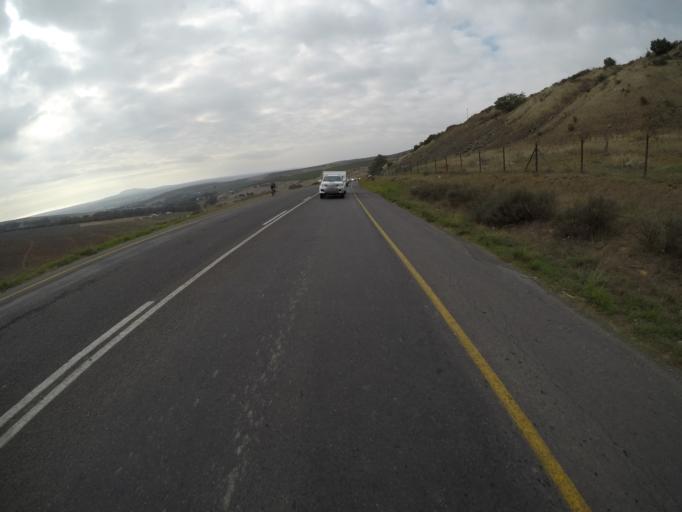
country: ZA
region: Western Cape
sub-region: City of Cape Town
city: Sunset Beach
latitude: -33.8322
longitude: 18.5897
